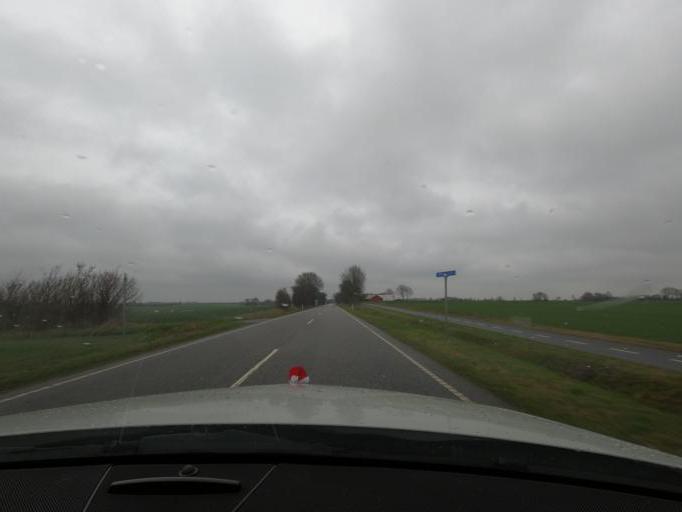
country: DK
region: South Denmark
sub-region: Haderslev Kommune
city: Starup
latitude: 55.2548
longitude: 9.6145
